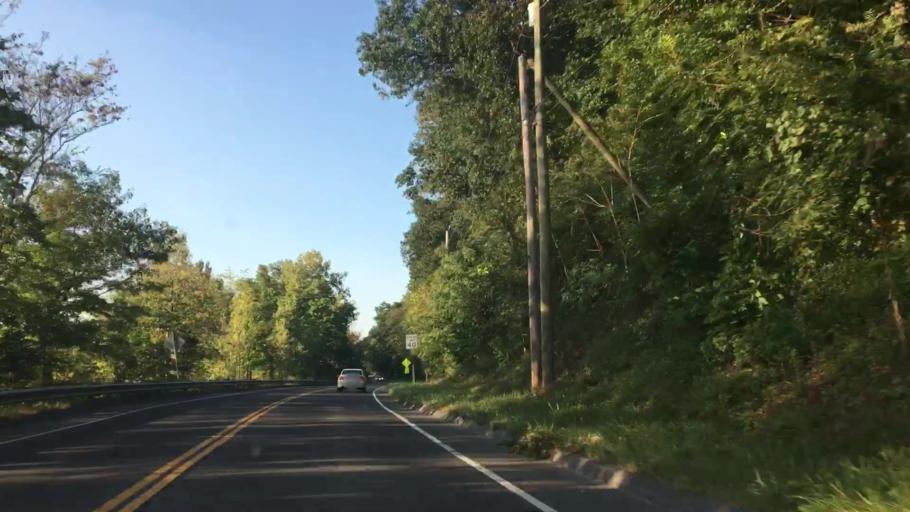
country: US
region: Connecticut
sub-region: Litchfield County
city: New Milford
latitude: 41.5511
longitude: -73.4056
